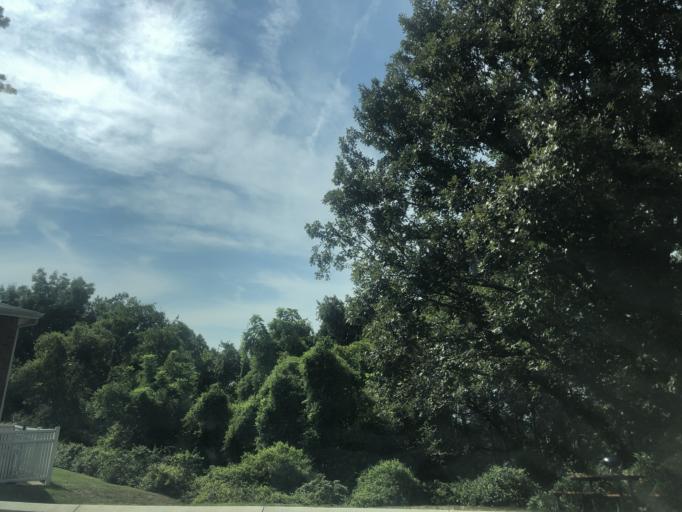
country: US
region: Tennessee
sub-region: Rutherford County
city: La Vergne
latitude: 36.0808
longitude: -86.6616
